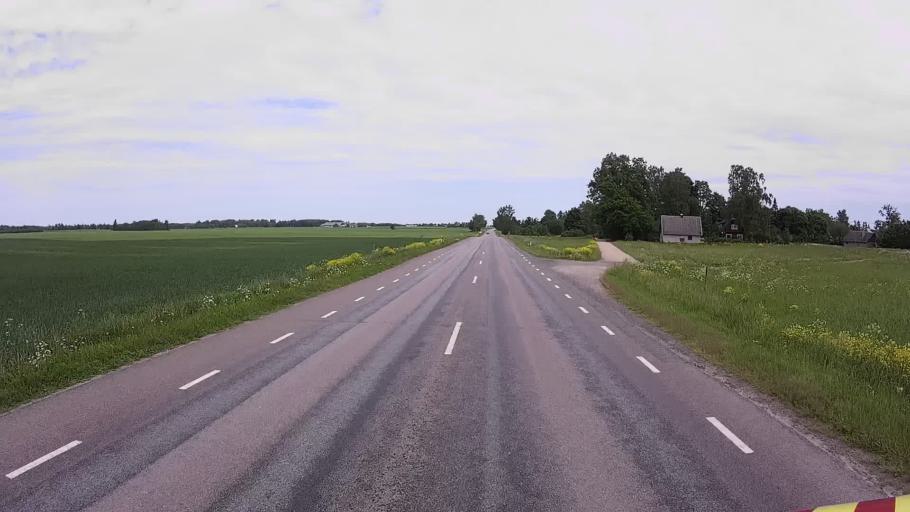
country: EE
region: Laeaene-Virumaa
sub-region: Vaeike-Maarja vald
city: Vaike-Maarja
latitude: 59.1508
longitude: 26.2637
